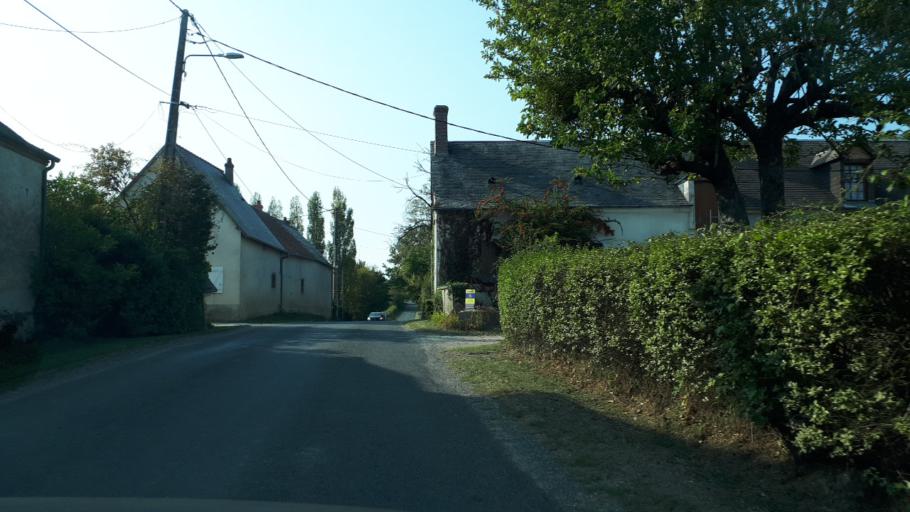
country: FR
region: Centre
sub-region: Departement du Cher
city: Menetou-Salon
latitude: 47.2220
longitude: 2.5318
